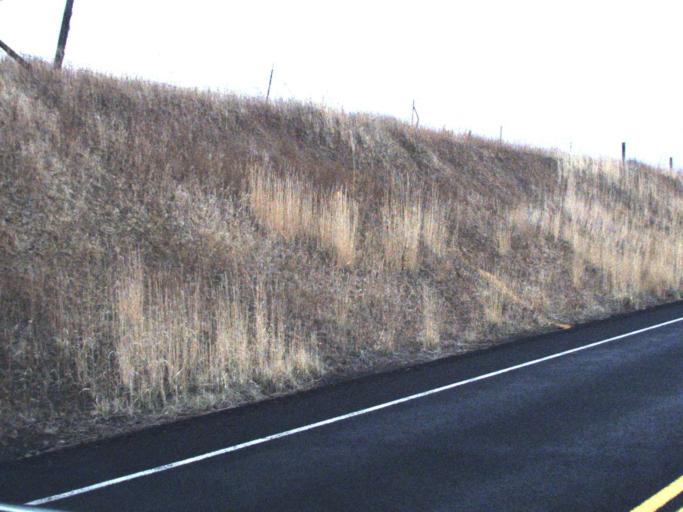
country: US
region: Washington
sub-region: Lincoln County
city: Davenport
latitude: 47.8105
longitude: -118.1789
